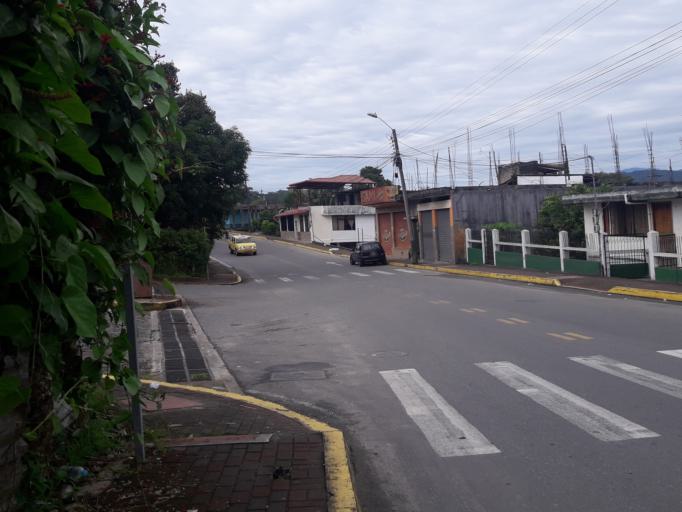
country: EC
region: Napo
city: Tena
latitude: -0.9996
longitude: -77.8140
